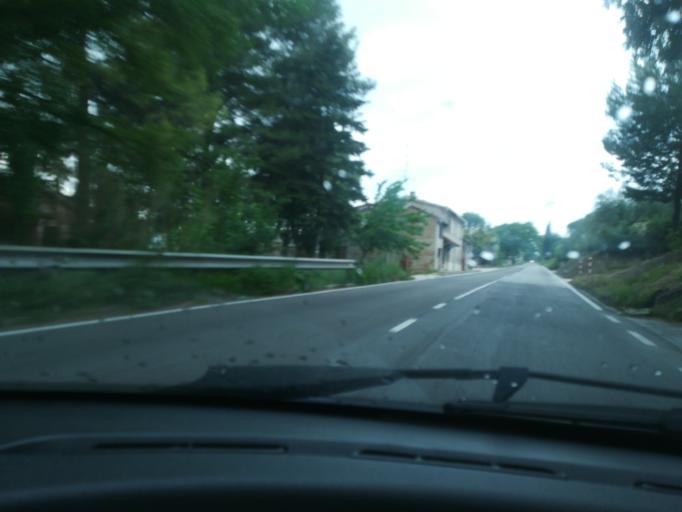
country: IT
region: The Marches
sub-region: Provincia di Macerata
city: Treia
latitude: 43.2989
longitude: 13.3175
